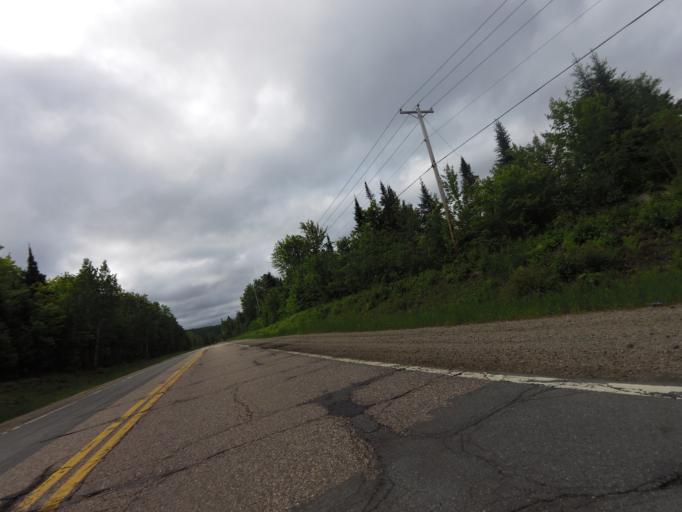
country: CA
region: Quebec
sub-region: Outaouais
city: Shawville
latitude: 45.8234
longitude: -76.4610
